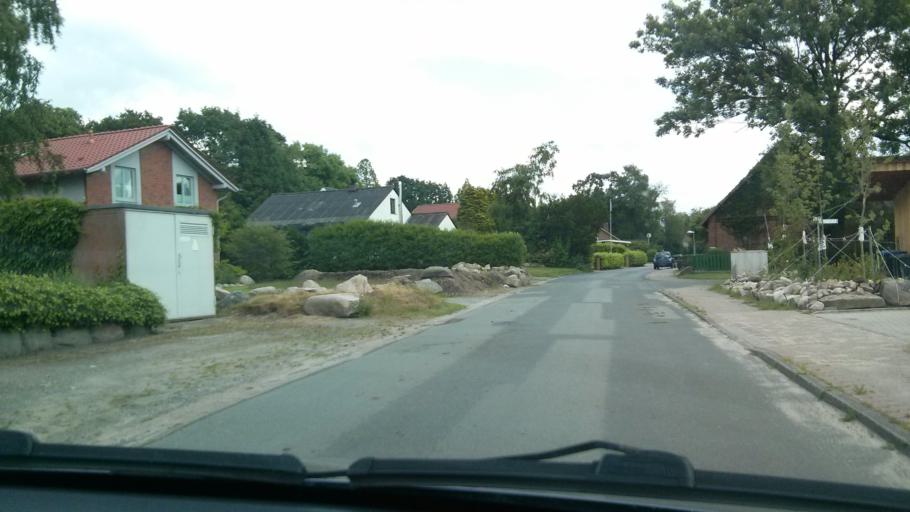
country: DE
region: Lower Saxony
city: Loxstedt
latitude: 53.4907
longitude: 8.6886
